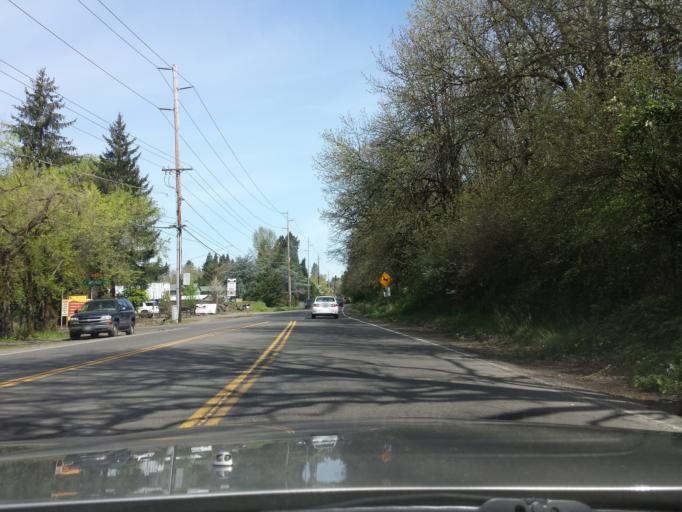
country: US
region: Oregon
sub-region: Washington County
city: Aloha
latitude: 45.4971
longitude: -122.8523
